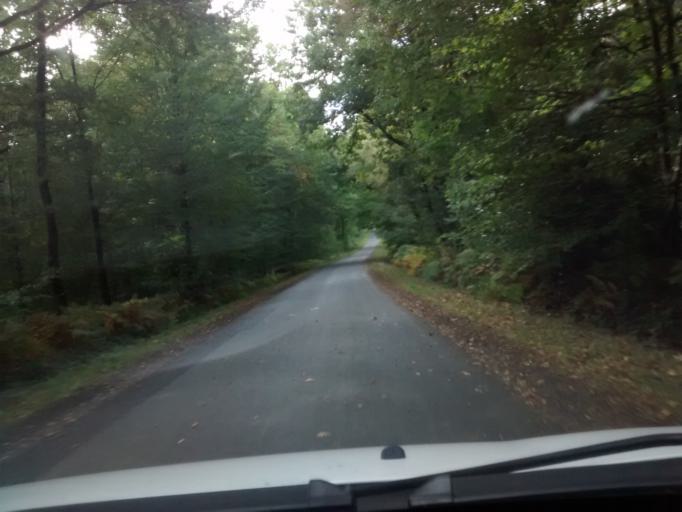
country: FR
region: Brittany
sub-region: Departement d'Ille-et-Vilaine
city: Chateaubourg
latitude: 48.1344
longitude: -1.3803
